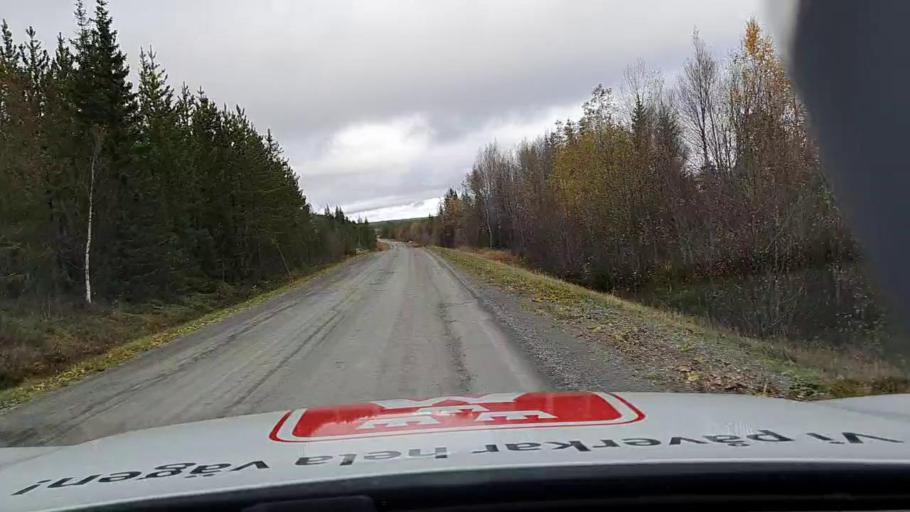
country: SE
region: Jaemtland
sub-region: Krokoms Kommun
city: Valla
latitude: 63.0569
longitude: 13.9631
